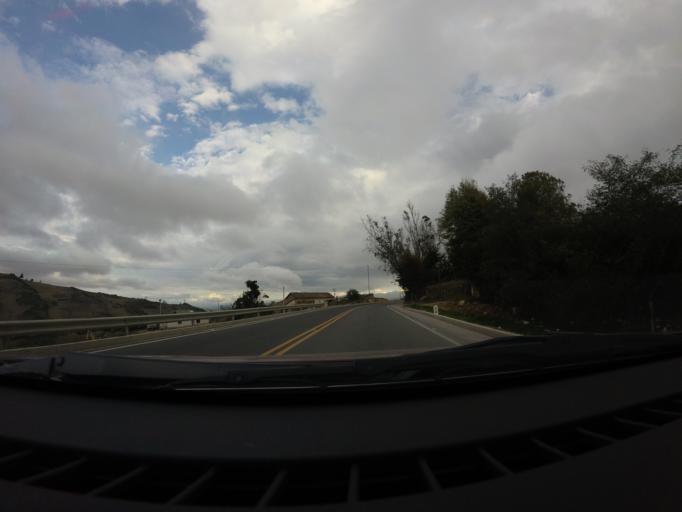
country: CO
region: Boyaca
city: Cucaita
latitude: 5.5610
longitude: -73.4124
